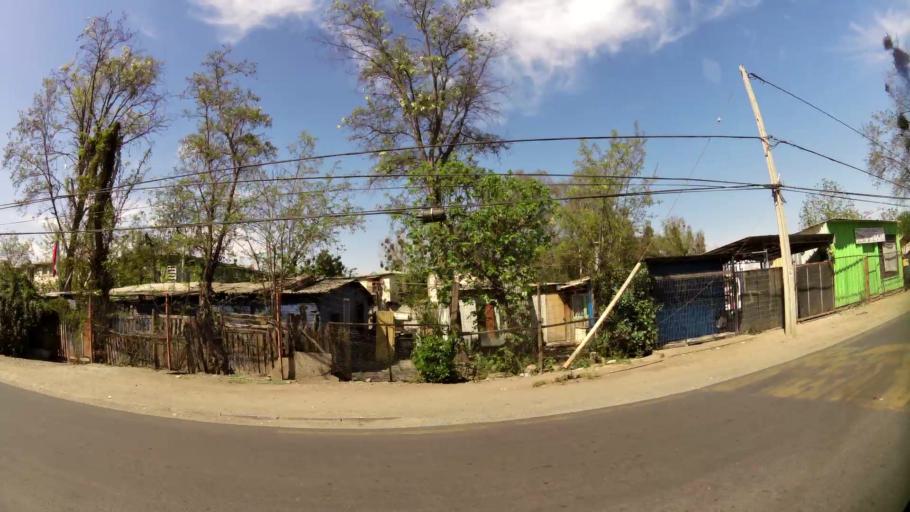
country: CL
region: Santiago Metropolitan
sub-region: Provincia de Santiago
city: Lo Prado
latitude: -33.3996
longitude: -70.7406
